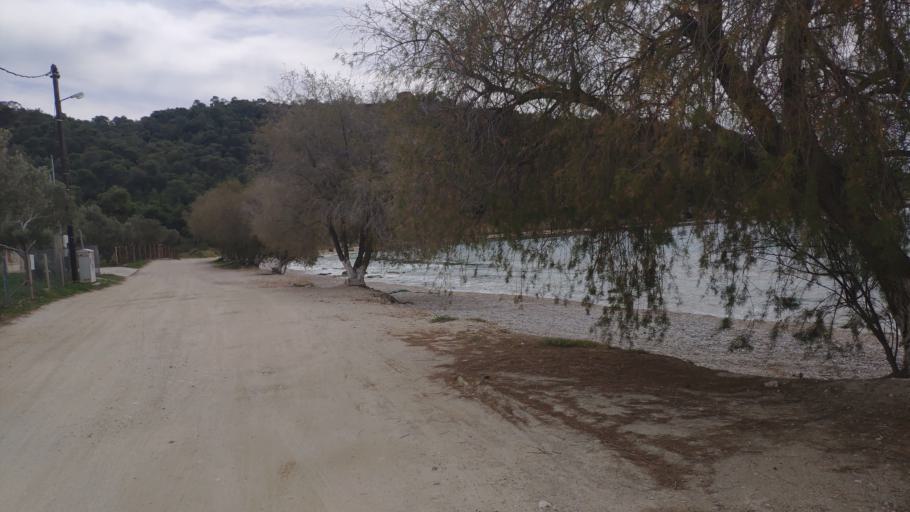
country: GR
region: Attica
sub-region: Nomos Piraios
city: Aianteio
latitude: 37.9004
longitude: 23.4089
